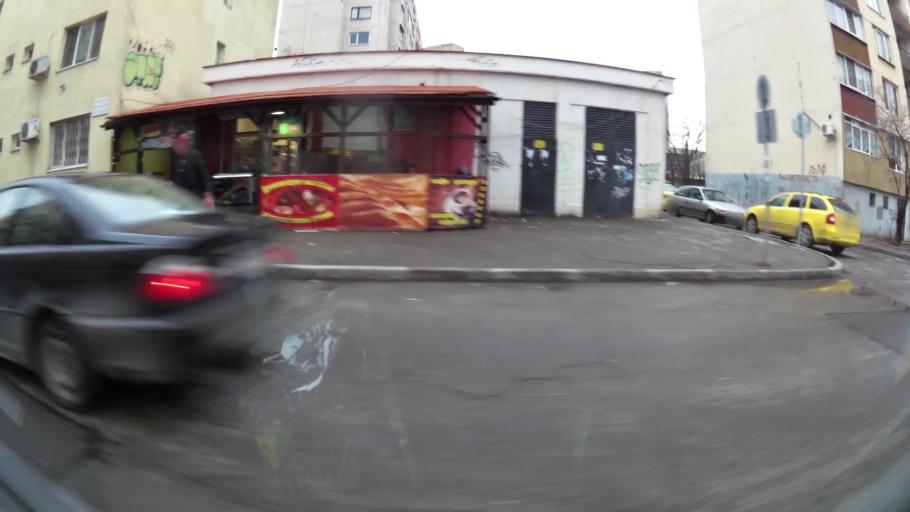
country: BG
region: Sofia-Capital
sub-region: Stolichna Obshtina
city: Sofia
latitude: 42.7274
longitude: 23.2975
